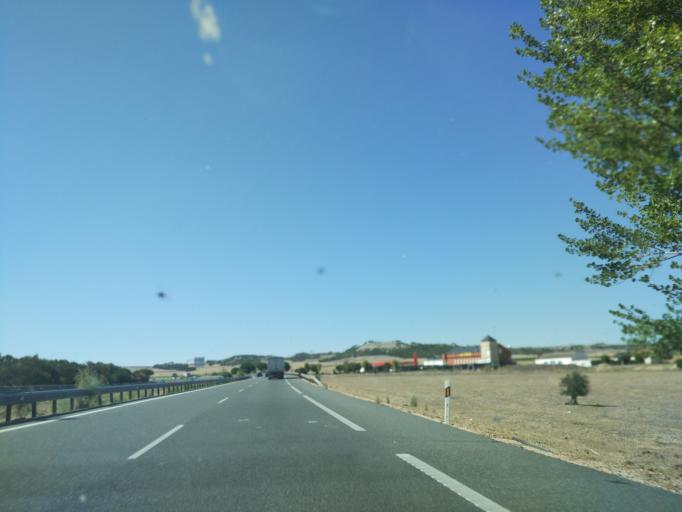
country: ES
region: Castille and Leon
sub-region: Provincia de Valladolid
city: Vega de Valdetronco
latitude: 41.5947
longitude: -5.1212
